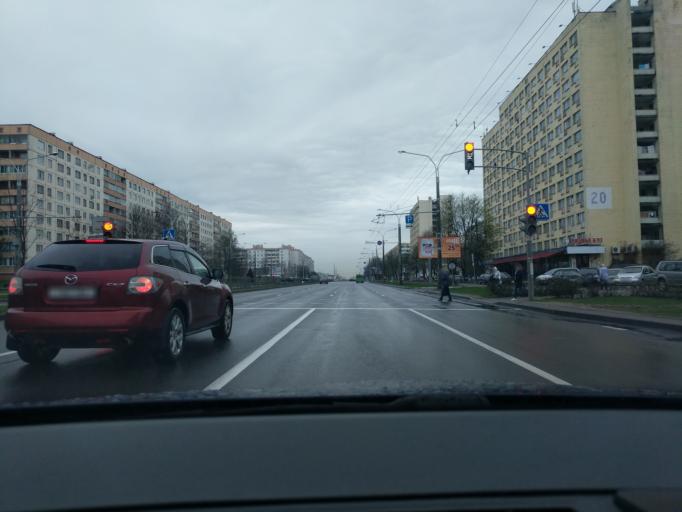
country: BY
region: Minsk
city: Novoye Medvezhino
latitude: 53.9000
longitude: 27.4970
